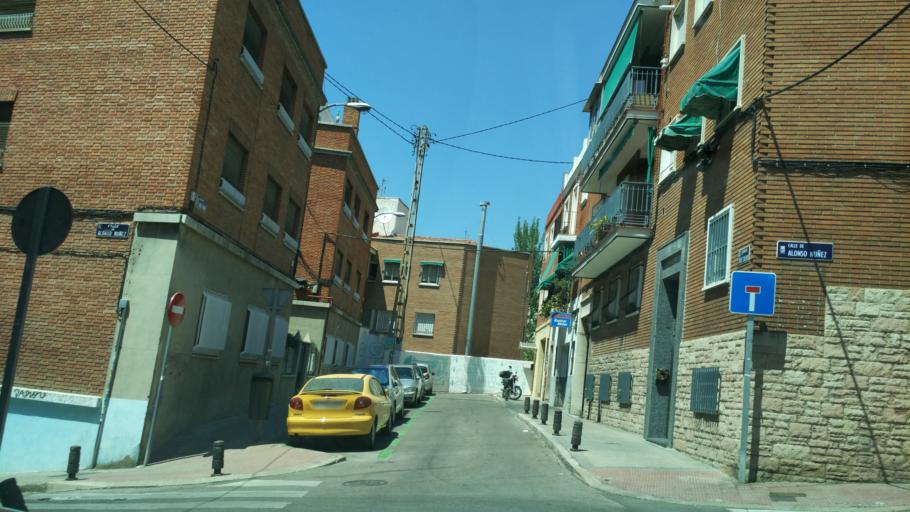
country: ES
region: Madrid
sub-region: Provincia de Madrid
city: Tetuan de las Victorias
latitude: 40.4585
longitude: -3.7083
